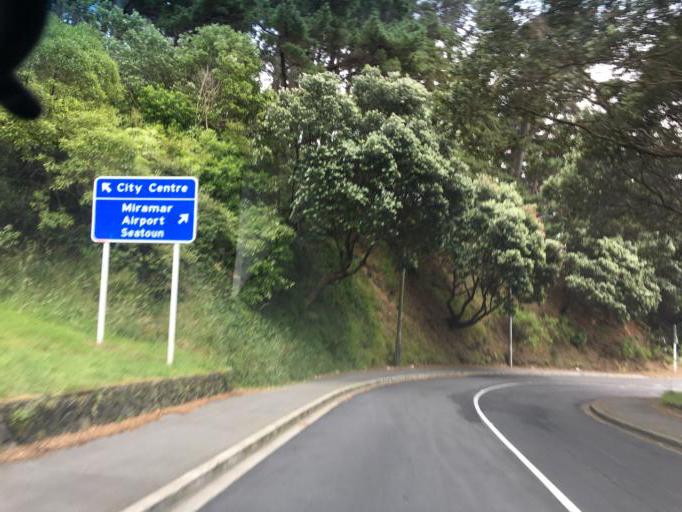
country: NZ
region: Wellington
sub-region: Wellington City
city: Wellington
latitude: -41.3124
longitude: 174.7899
